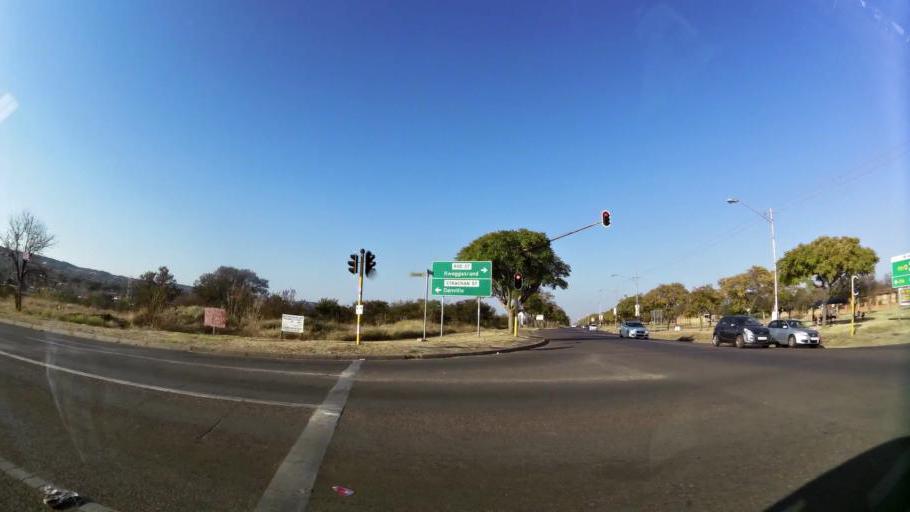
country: ZA
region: Gauteng
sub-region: City of Tshwane Metropolitan Municipality
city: Pretoria
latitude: -25.7510
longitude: 28.1203
